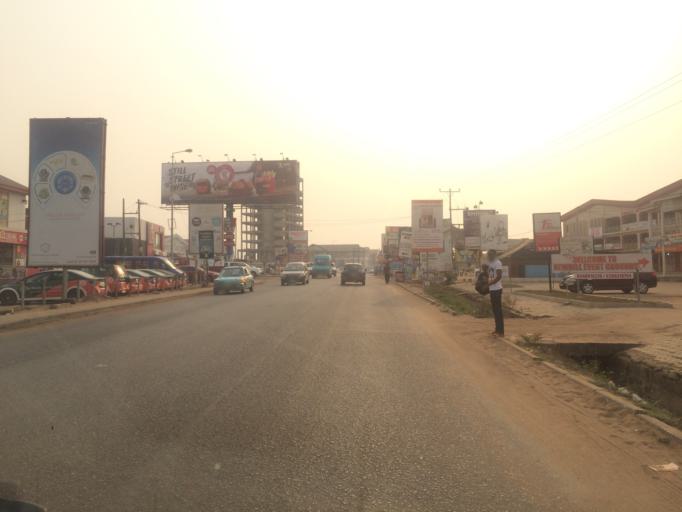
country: GH
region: Greater Accra
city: Nungua
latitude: 5.6250
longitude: -0.0768
